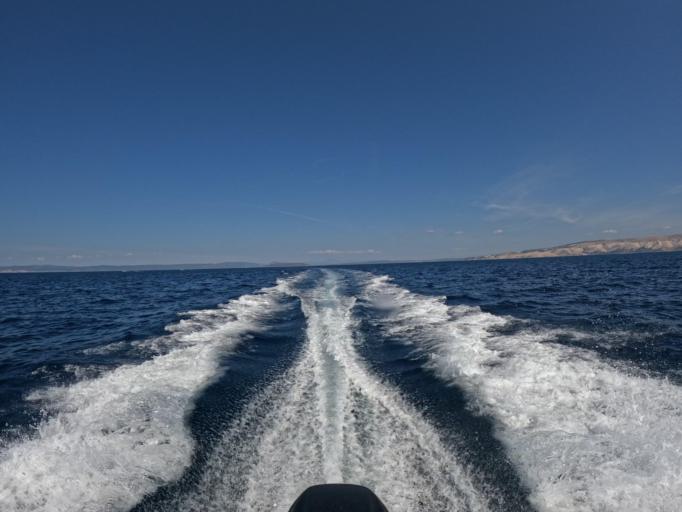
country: HR
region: Primorsko-Goranska
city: Lopar
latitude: 44.8841
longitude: 14.6532
